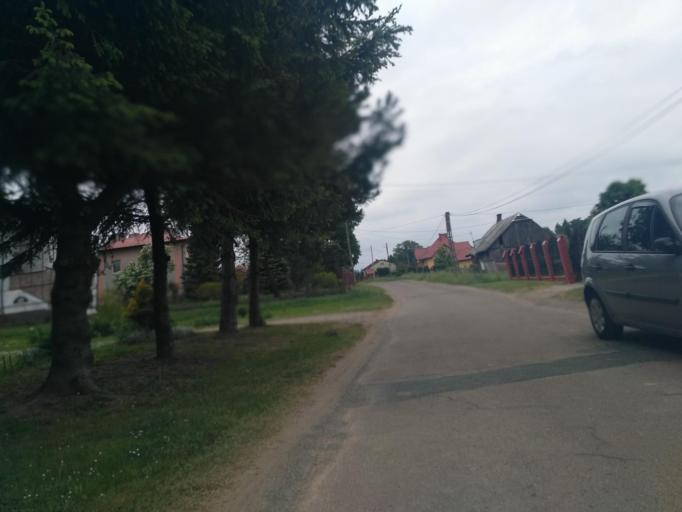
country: PL
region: Subcarpathian Voivodeship
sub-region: Powiat krosnienski
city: Chorkowka
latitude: 49.6624
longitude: 21.7181
